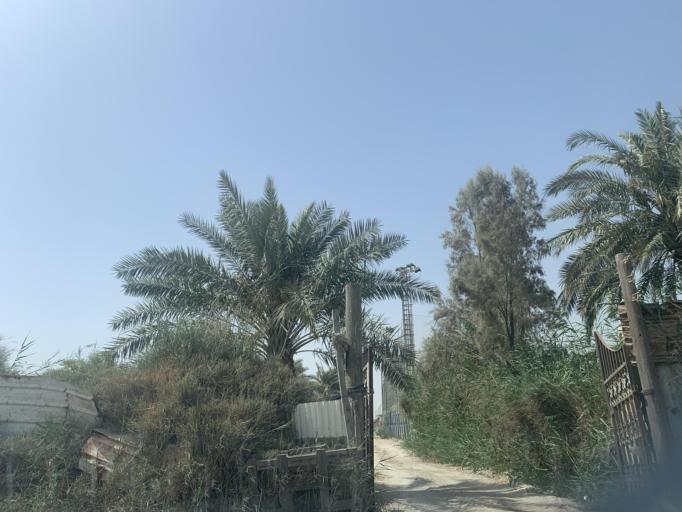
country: BH
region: Manama
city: Jidd Hafs
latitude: 26.2024
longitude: 50.5411
